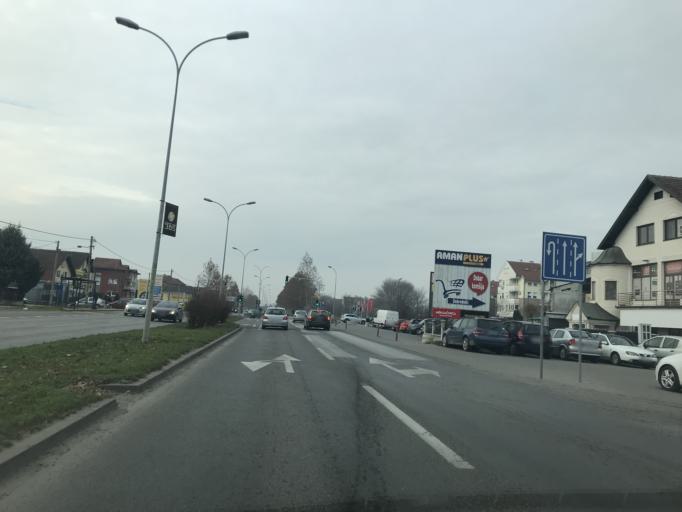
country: RS
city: Veternik
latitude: 45.2476
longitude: 19.7645
